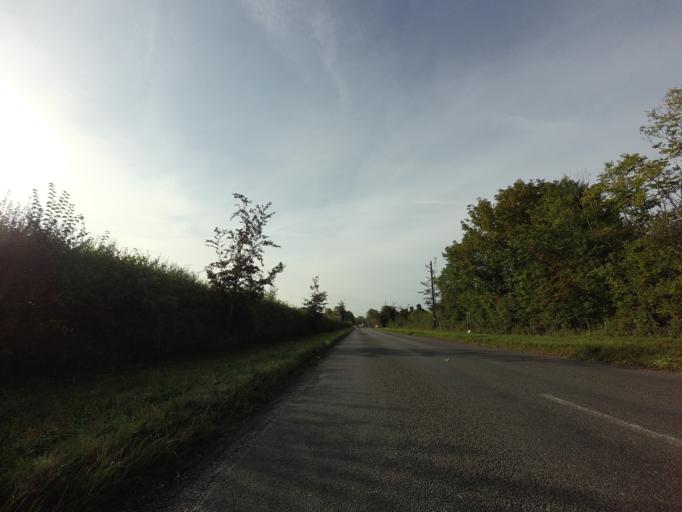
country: GB
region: England
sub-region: Cambridgeshire
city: Harston
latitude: 52.1277
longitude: 0.0998
